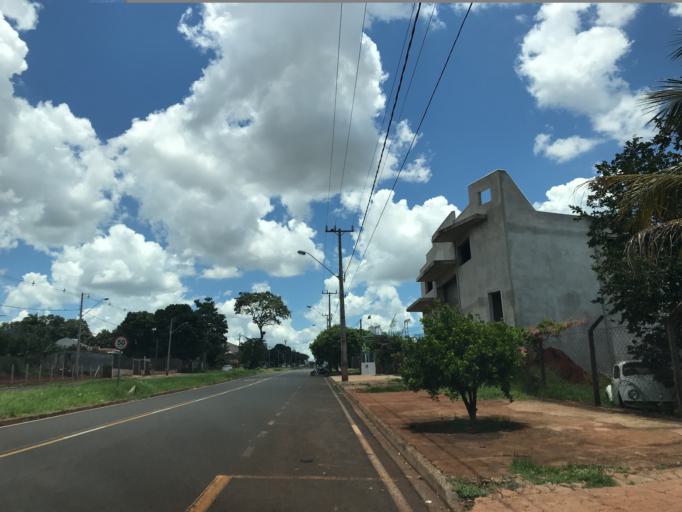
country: BR
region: Parana
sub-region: Maringa
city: Maringa
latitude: -23.3864
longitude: -51.9122
